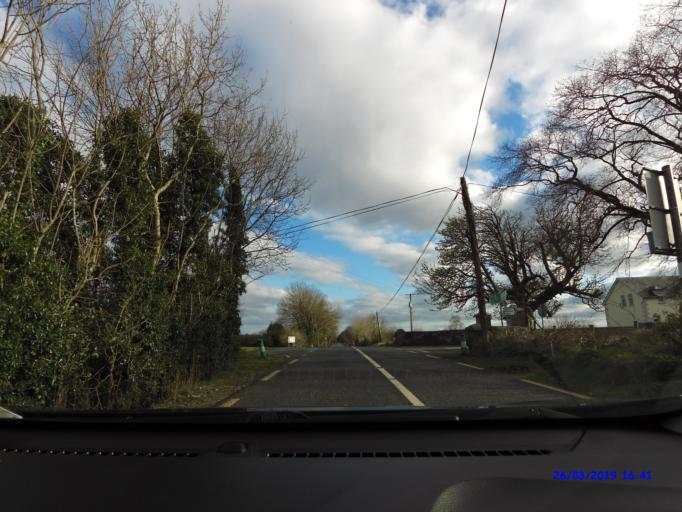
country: IE
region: Connaught
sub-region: Maigh Eo
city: Ballyhaunis
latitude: 53.8771
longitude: -8.7759
